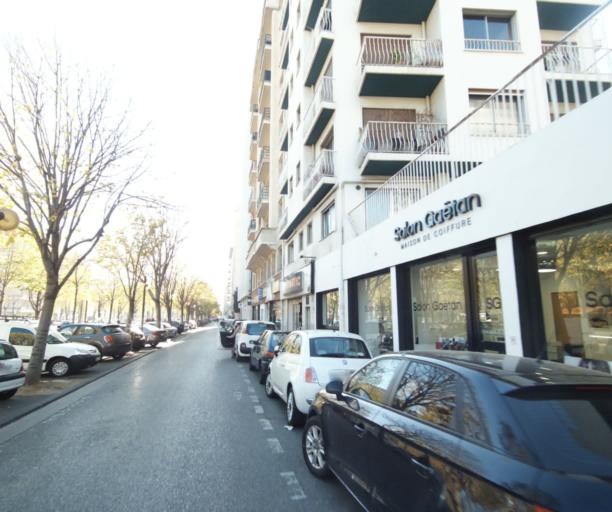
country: FR
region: Provence-Alpes-Cote d'Azur
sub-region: Departement des Bouches-du-Rhone
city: Marseille 08
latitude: 43.2783
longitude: 5.3877
